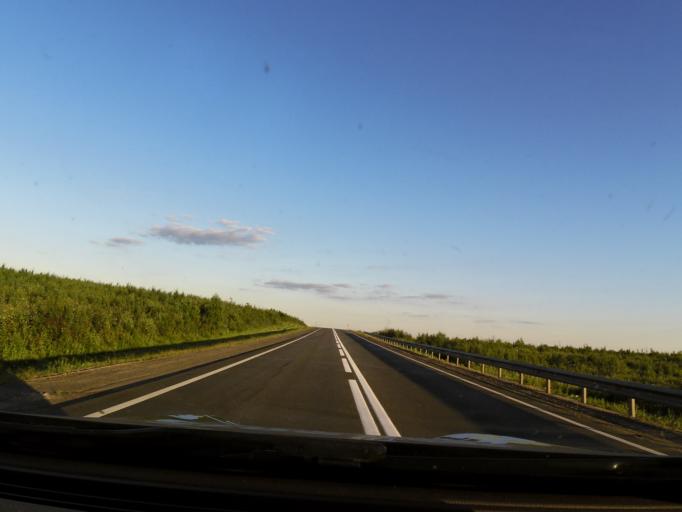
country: RU
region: Jaroslavl
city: Prechistoye
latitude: 58.6243
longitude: 40.3309
